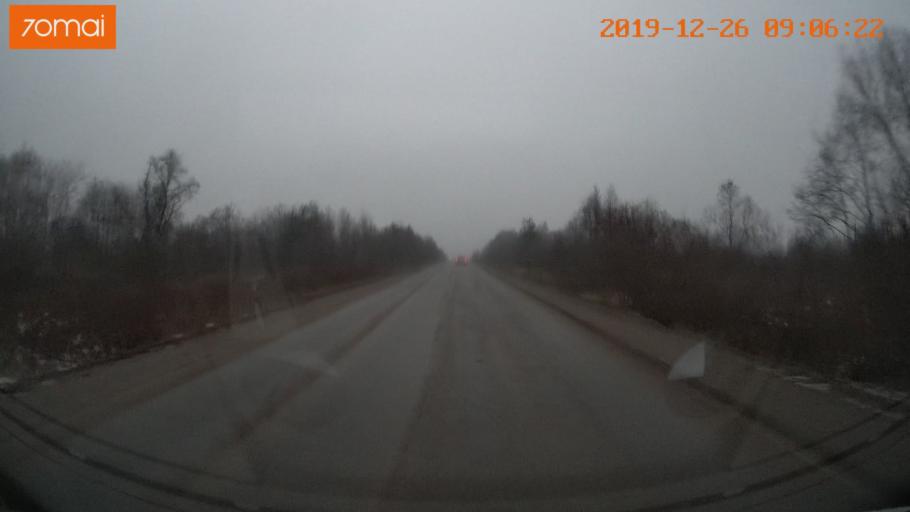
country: RU
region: Vologda
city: Gryazovets
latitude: 58.8356
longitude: 40.2535
